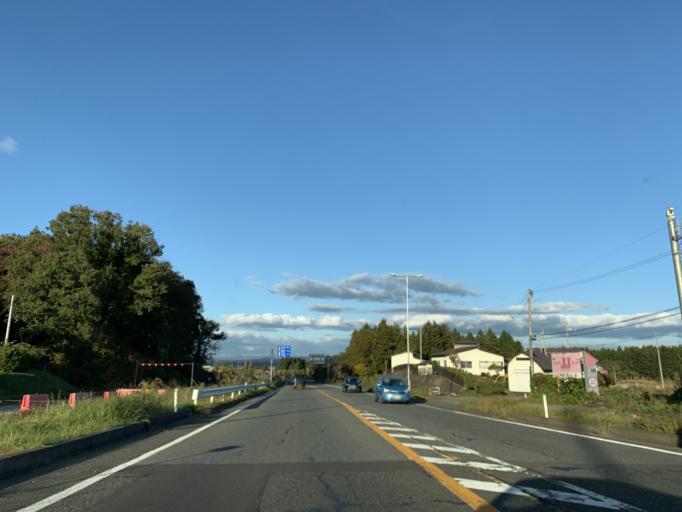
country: JP
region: Iwate
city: Kitakami
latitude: 39.2370
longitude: 141.0955
